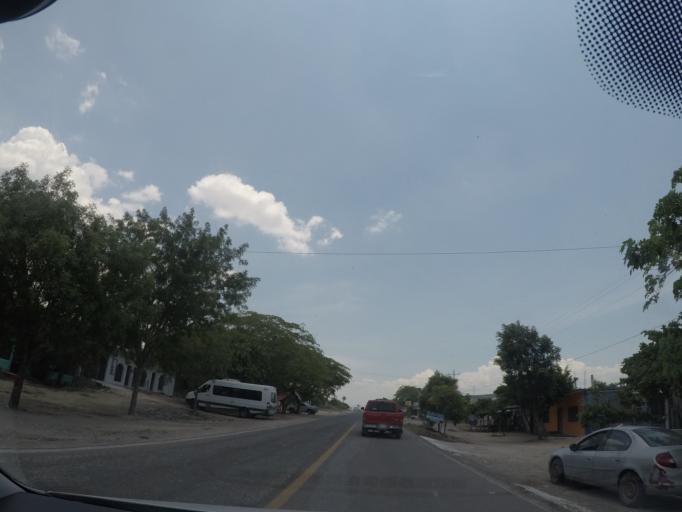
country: MX
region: Oaxaca
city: Santa Maria Jalapa del Marques
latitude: 16.4400
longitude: -95.4530
